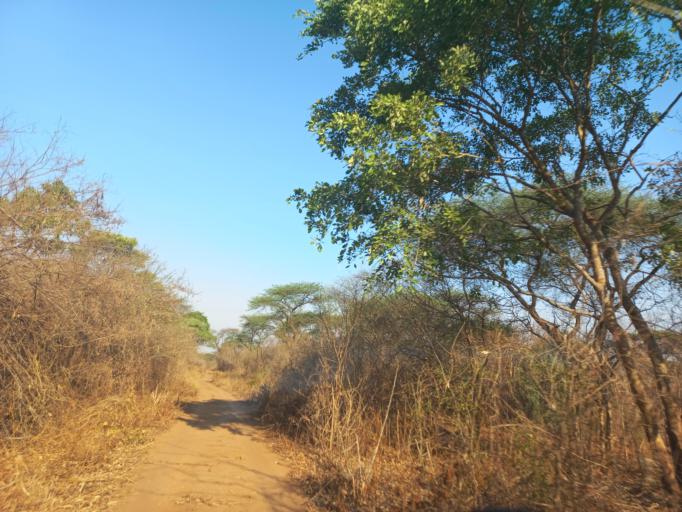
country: ZM
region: Lusaka
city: Luangwa
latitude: -15.4175
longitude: 30.2477
